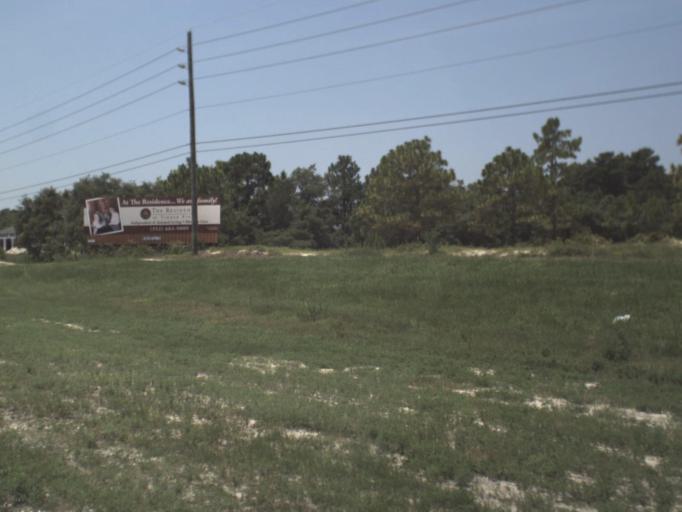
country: US
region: Florida
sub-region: Hernando County
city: North Weeki Wachee
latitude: 28.5504
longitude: -82.5633
